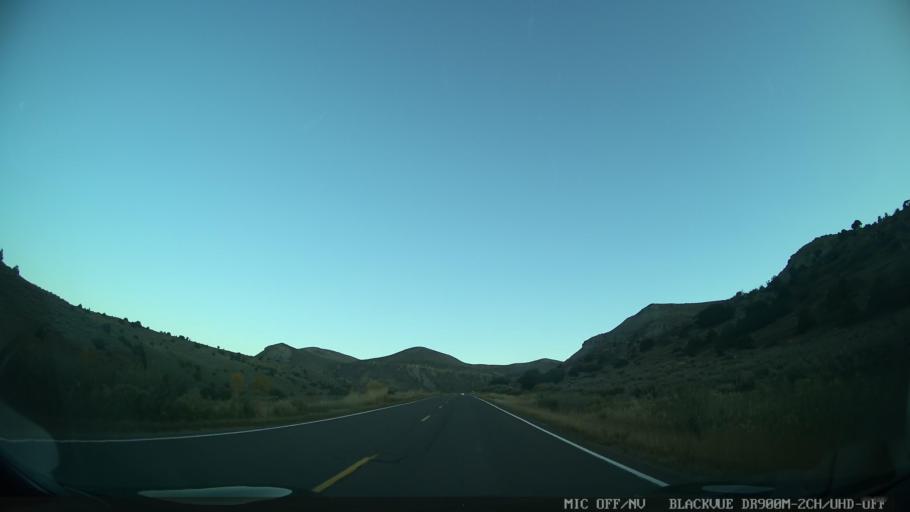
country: US
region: Colorado
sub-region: Eagle County
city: Edwards
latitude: 39.7661
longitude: -106.6788
